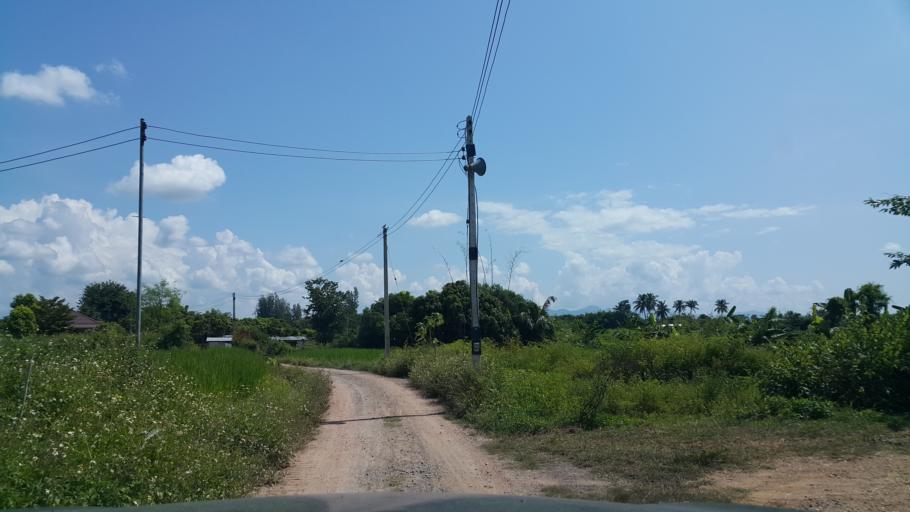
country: TH
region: Chiang Mai
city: Chom Thong
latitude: 18.4180
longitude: 98.6830
